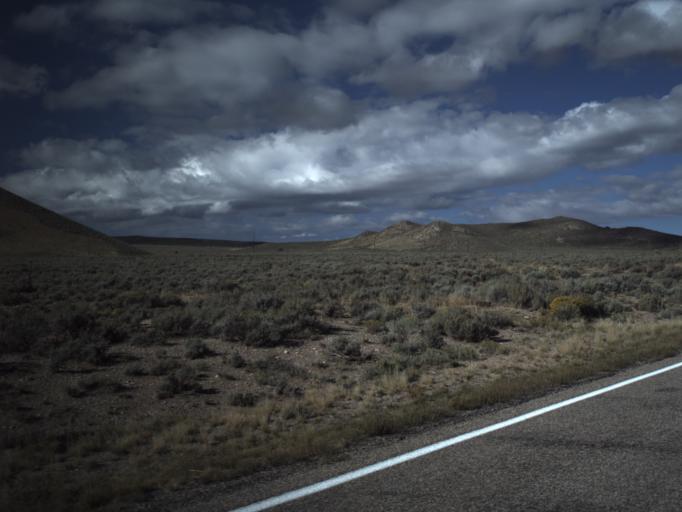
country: US
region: Utah
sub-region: Beaver County
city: Milford
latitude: 38.4198
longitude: -113.0961
